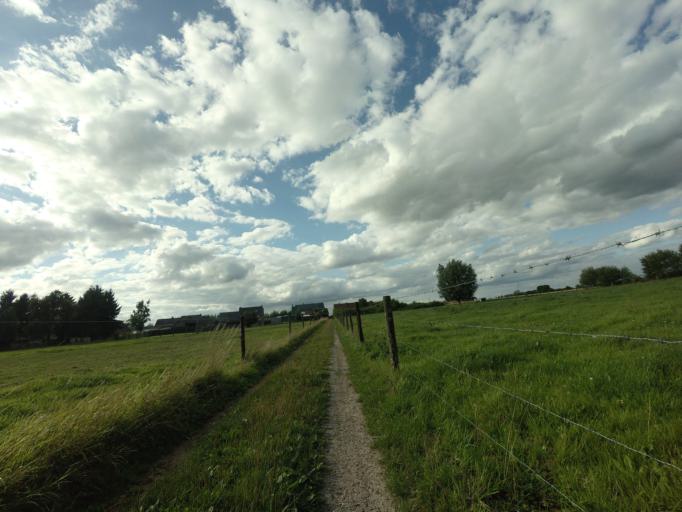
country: BE
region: Flanders
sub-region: Provincie Vlaams-Brabant
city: Kapelle-op-den-Bos
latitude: 50.9859
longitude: 4.3698
